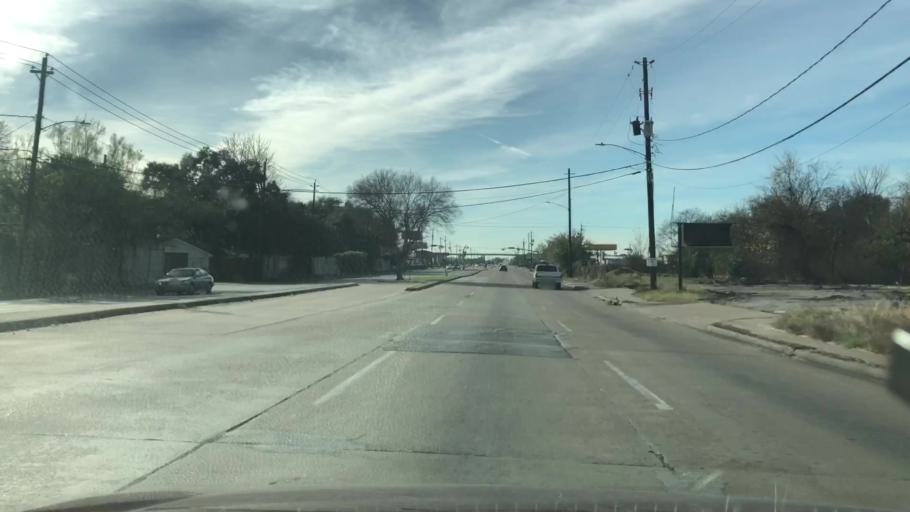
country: US
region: Texas
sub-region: Harris County
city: Bellaire
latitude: 29.6598
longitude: -95.4642
